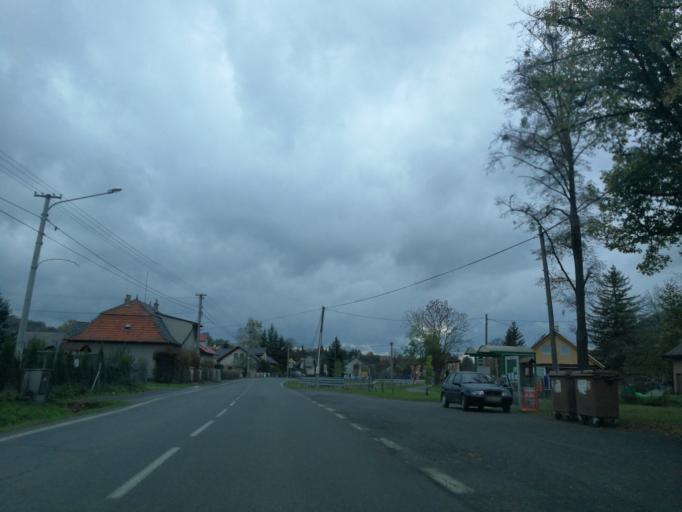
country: CZ
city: Stramberk
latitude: 49.5718
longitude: 18.1094
